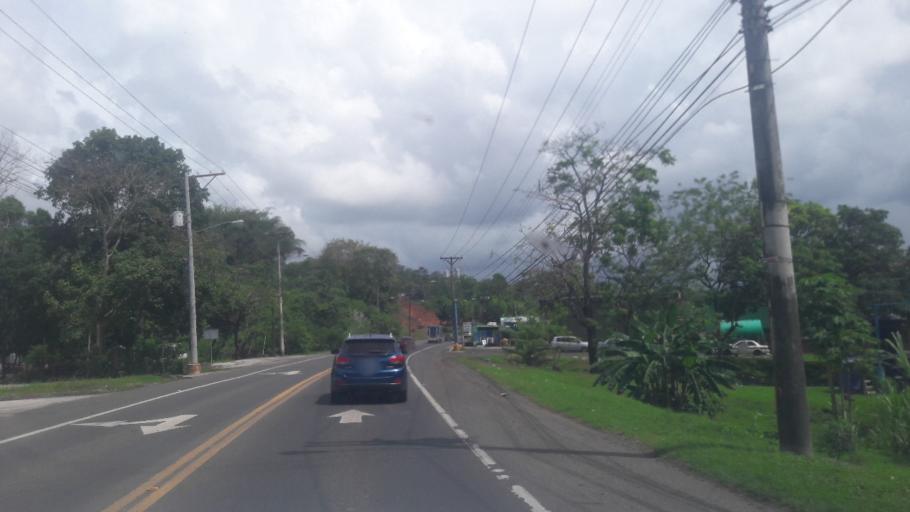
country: PA
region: Panama
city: Alcalde Diaz
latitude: 9.1268
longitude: -79.5845
